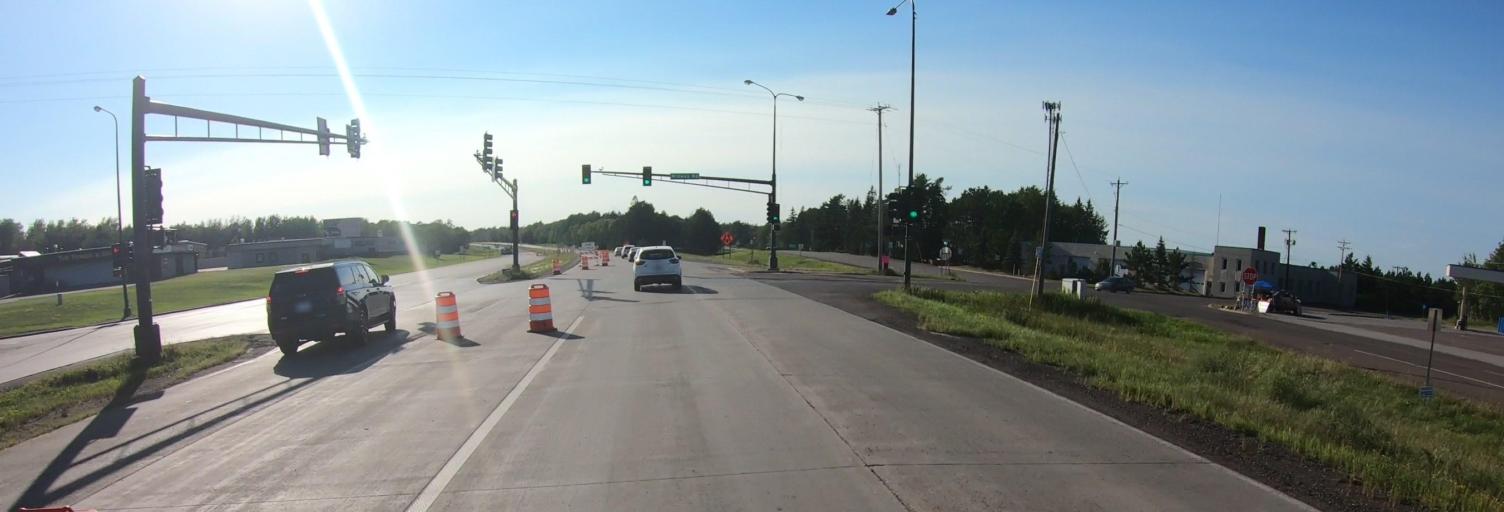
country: US
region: Minnesota
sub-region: Saint Louis County
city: Hermantown
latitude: 46.8505
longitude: -92.2832
